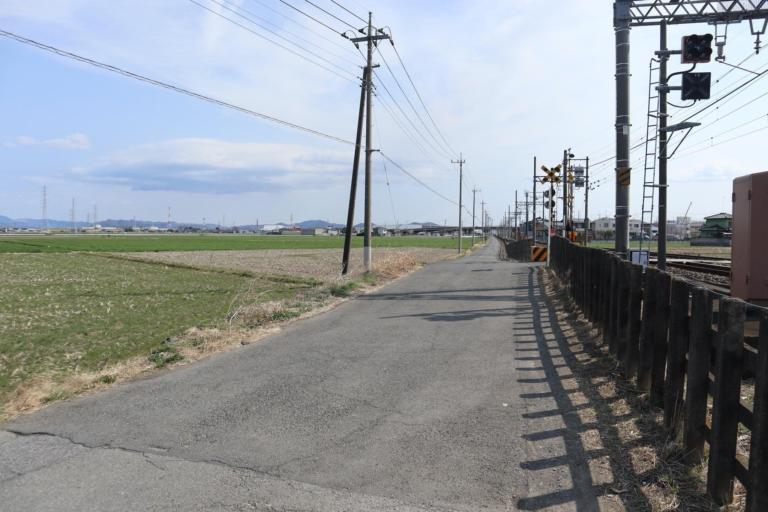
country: JP
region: Gunma
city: Tatebayashi
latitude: 36.2623
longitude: 139.5388
